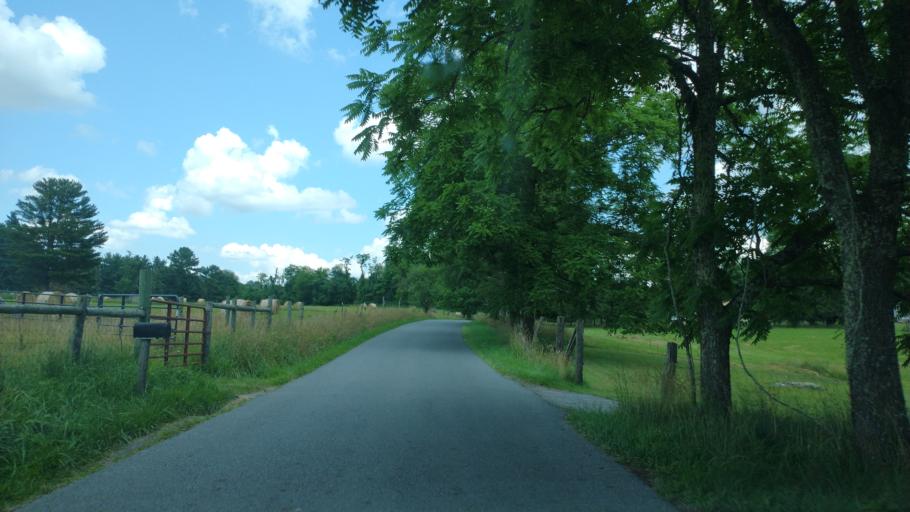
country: US
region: West Virginia
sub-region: Mercer County
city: Athens
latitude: 37.4569
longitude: -81.0343
